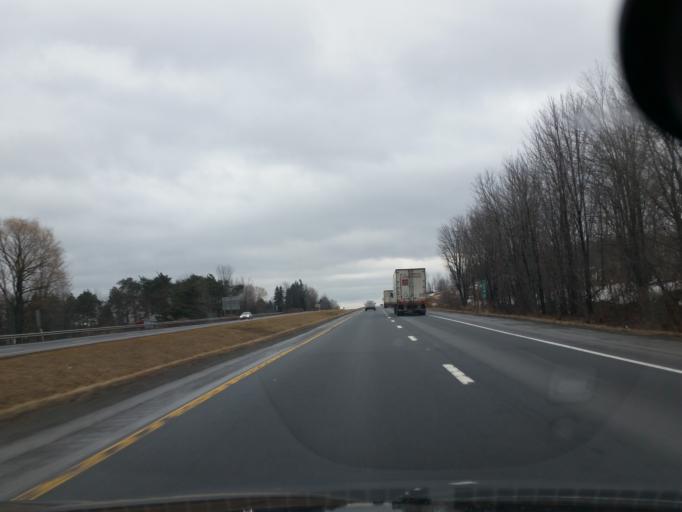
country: US
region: Pennsylvania
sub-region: Lackawanna County
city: Dalton
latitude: 41.6276
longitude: -75.6436
